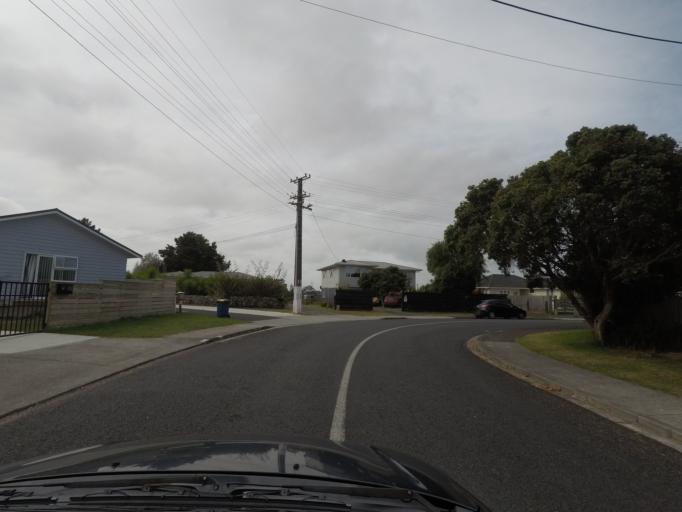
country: NZ
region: Auckland
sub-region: Auckland
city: Rosebank
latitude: -36.8906
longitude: 174.6669
